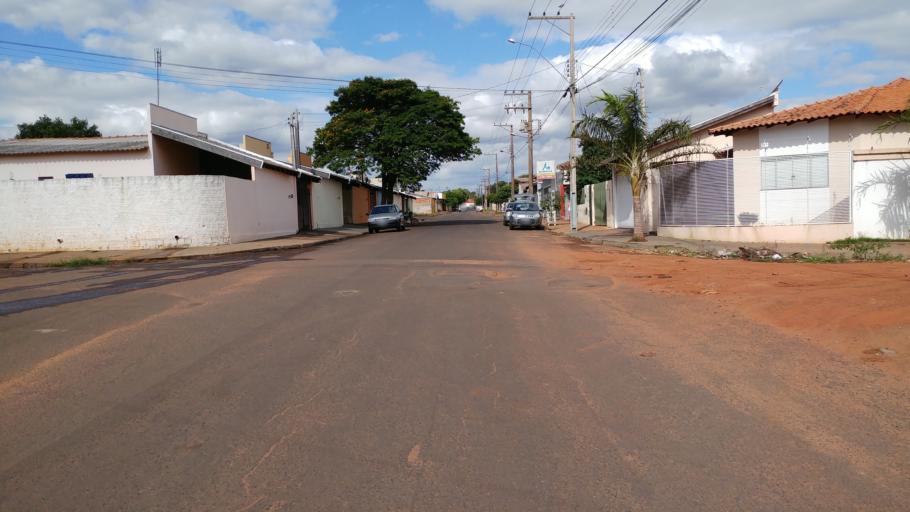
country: BR
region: Sao Paulo
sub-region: Paraguacu Paulista
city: Paraguacu Paulista
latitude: -22.4165
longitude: -50.5915
